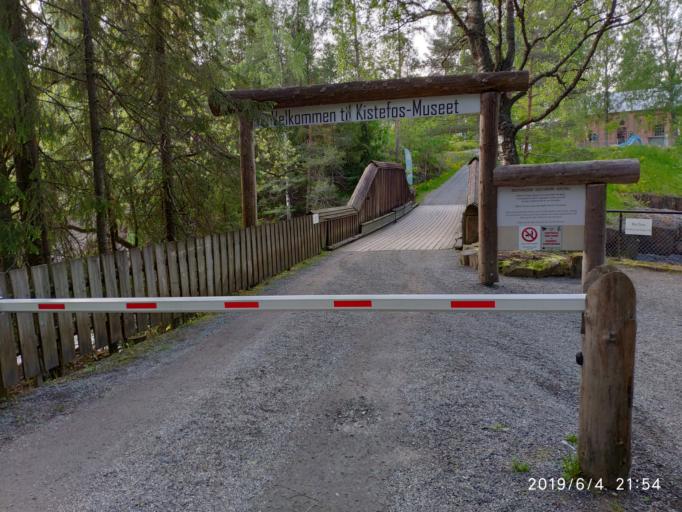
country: NO
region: Oppland
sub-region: Jevnaker
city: Jevnaker
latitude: 60.2207
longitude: 10.3688
